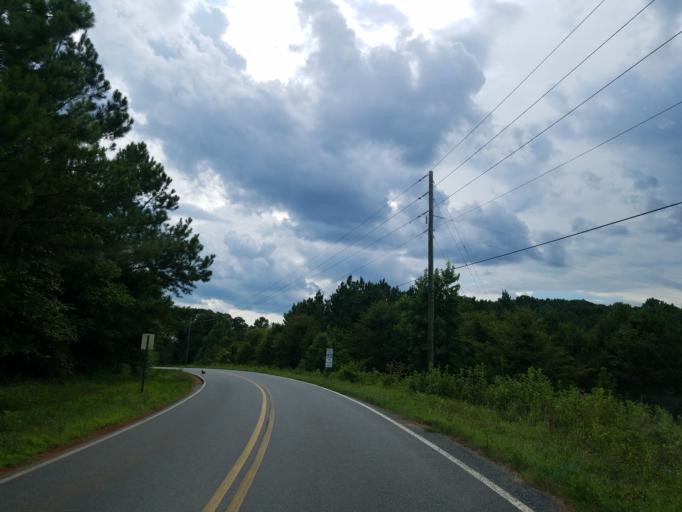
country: US
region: Georgia
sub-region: Bartow County
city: Rydal
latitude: 34.2748
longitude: -84.7686
